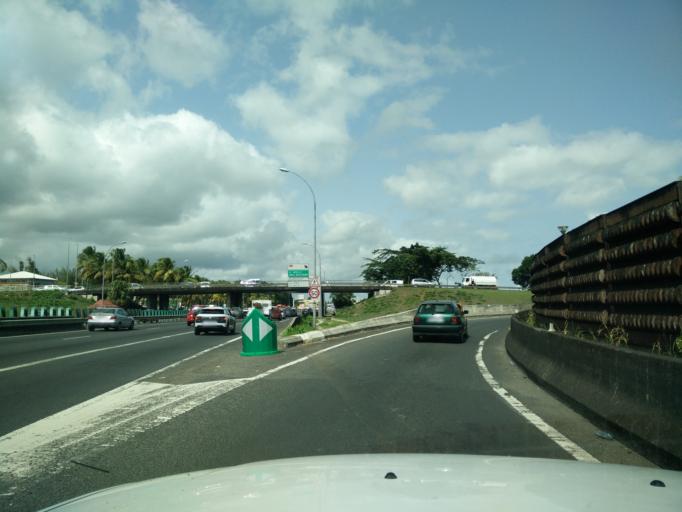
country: GP
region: Guadeloupe
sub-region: Guadeloupe
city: Baie-Mahault
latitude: 16.2540
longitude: -61.5719
